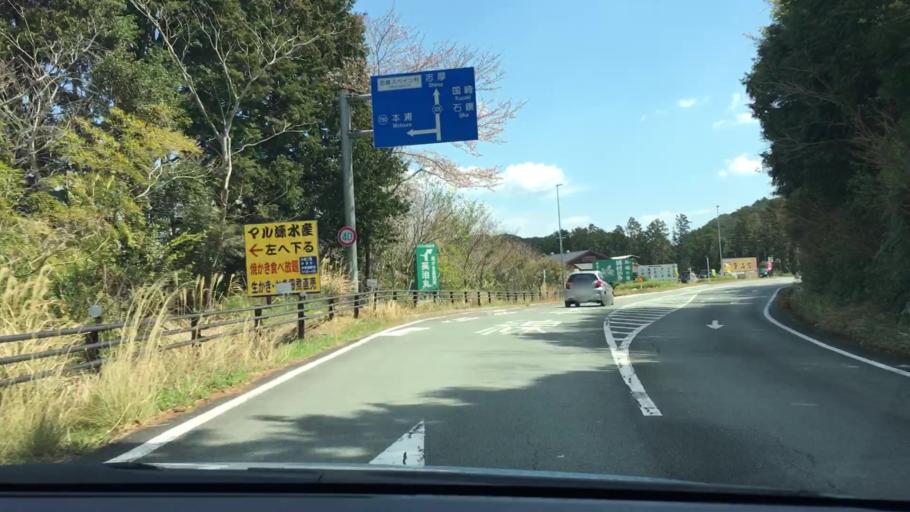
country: JP
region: Mie
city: Toba
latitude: 34.4417
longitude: 136.8911
